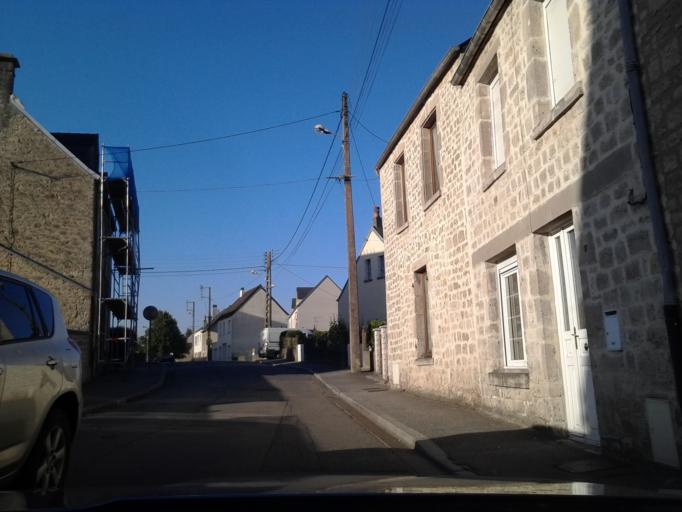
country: FR
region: Lower Normandy
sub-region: Departement de la Manche
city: Valognes
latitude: 49.5124
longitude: -1.4720
